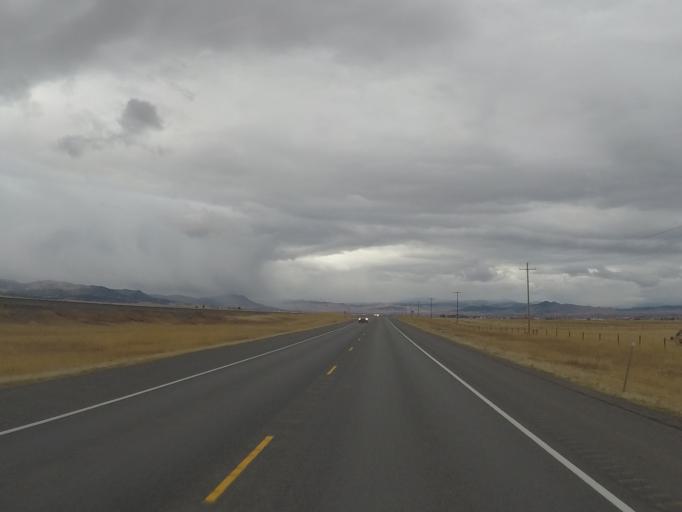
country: US
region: Montana
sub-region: Lewis and Clark County
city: East Helena
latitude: 46.5844
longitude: -111.8611
